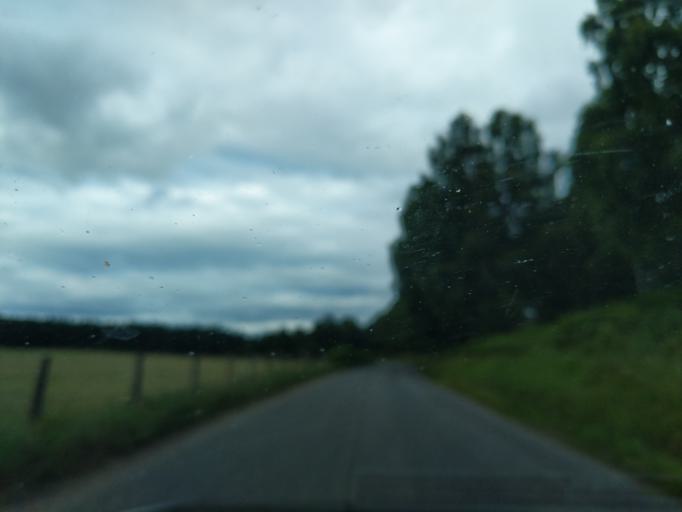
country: GB
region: Scotland
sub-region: Aberdeenshire
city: Aboyne
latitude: 57.0701
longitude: -2.8288
